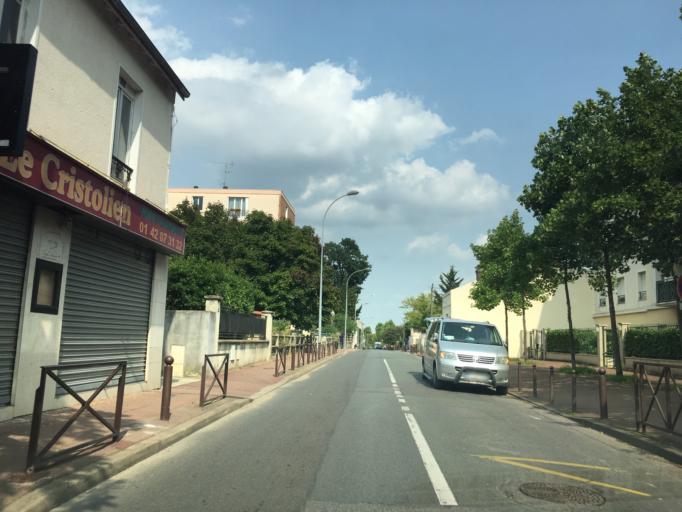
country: FR
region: Ile-de-France
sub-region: Departement du Val-de-Marne
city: Creteil
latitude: 48.8009
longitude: 2.4574
